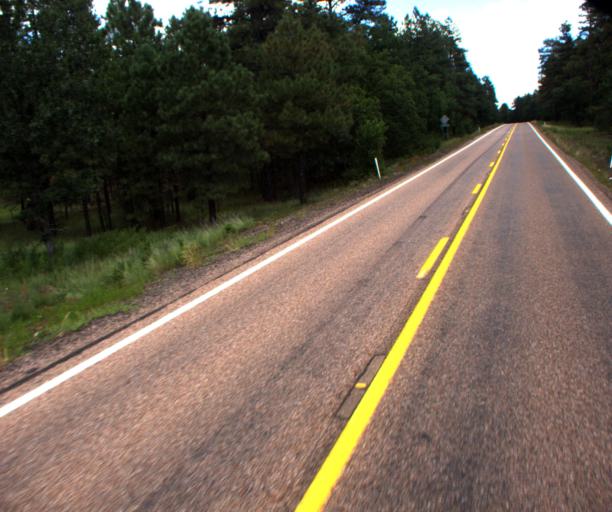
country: US
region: Arizona
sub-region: Navajo County
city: Pinetop-Lakeside
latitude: 34.0725
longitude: -109.8389
